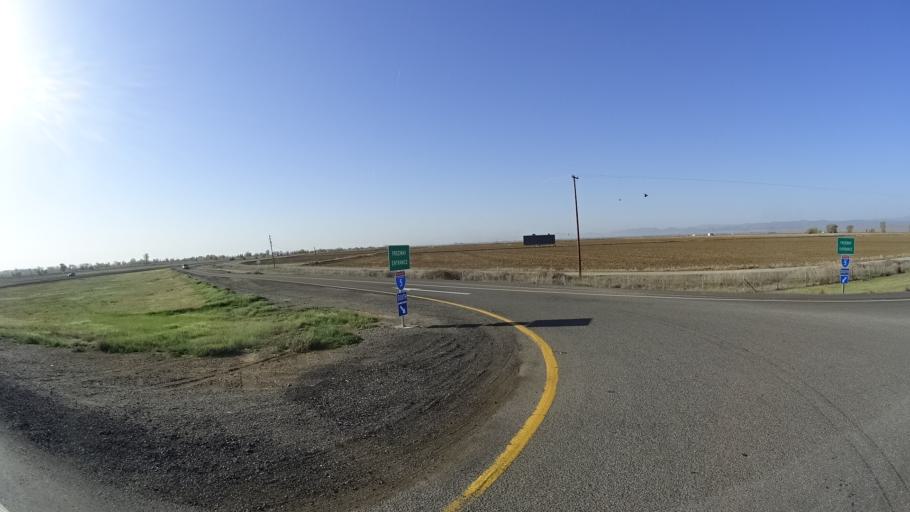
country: US
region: California
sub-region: Glenn County
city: Willows
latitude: 39.4072
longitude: -122.1976
